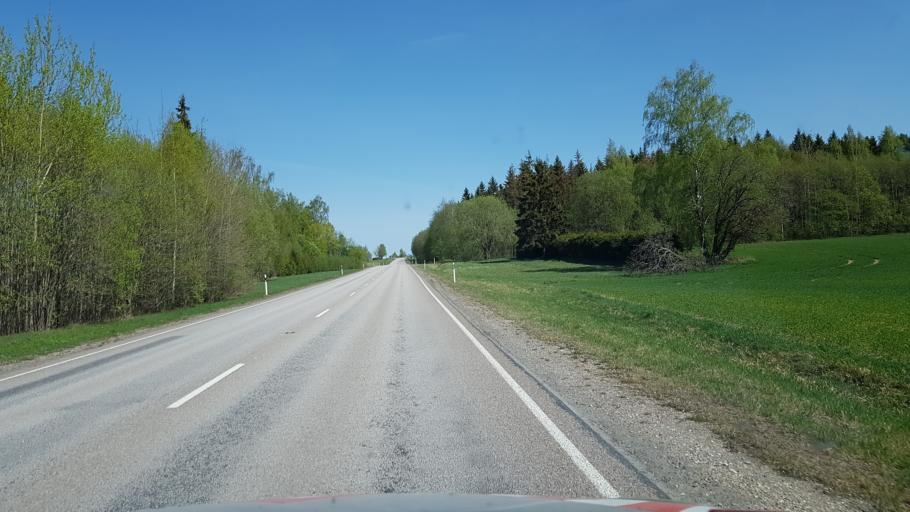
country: EE
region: Tartu
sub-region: Elva linn
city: Elva
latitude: 58.1031
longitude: 26.2342
